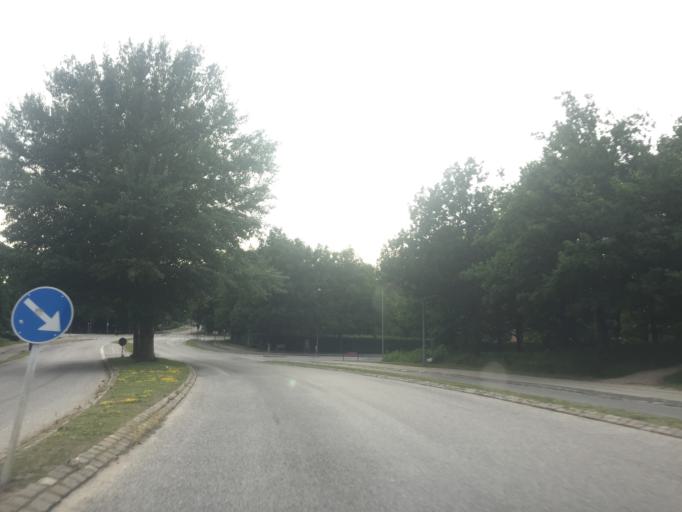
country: DK
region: Capital Region
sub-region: Lyngby-Tarbaek Kommune
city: Kongens Lyngby
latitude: 55.7865
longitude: 12.5169
